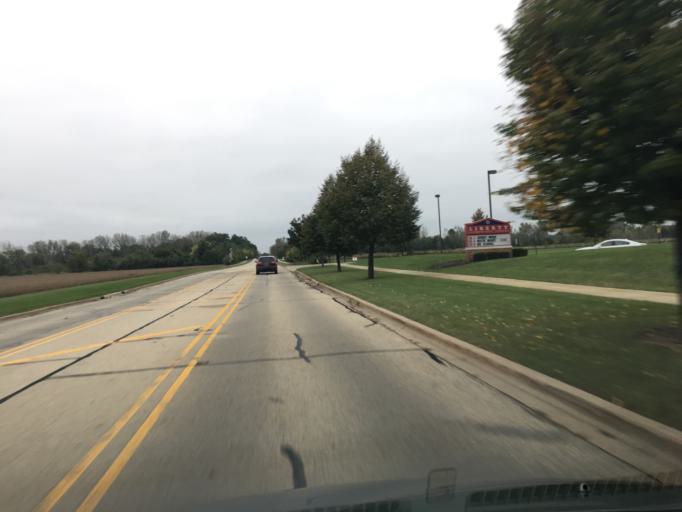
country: US
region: Illinois
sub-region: Will County
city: Plainfield
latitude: 41.6493
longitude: -88.1648
